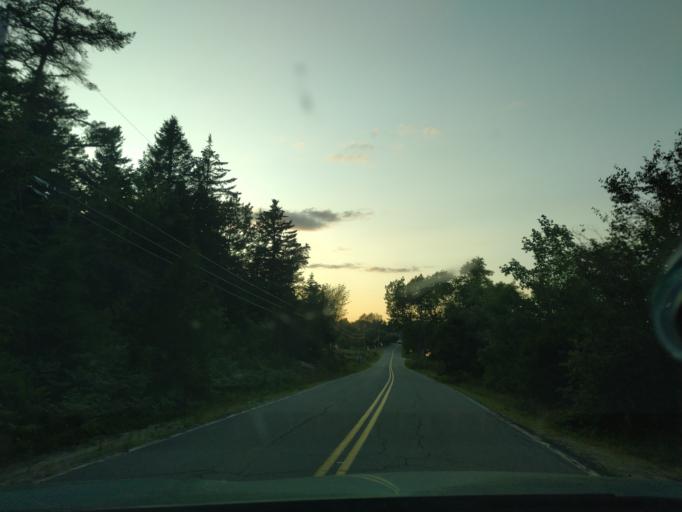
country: US
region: Maine
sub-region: Hancock County
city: Gouldsboro
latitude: 44.3845
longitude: -68.0371
